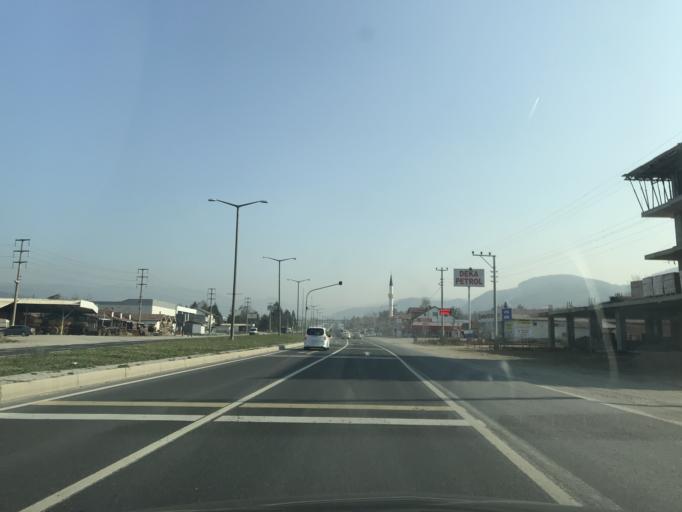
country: TR
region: Duzce
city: Kaynasli
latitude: 40.7788
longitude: 31.2873
